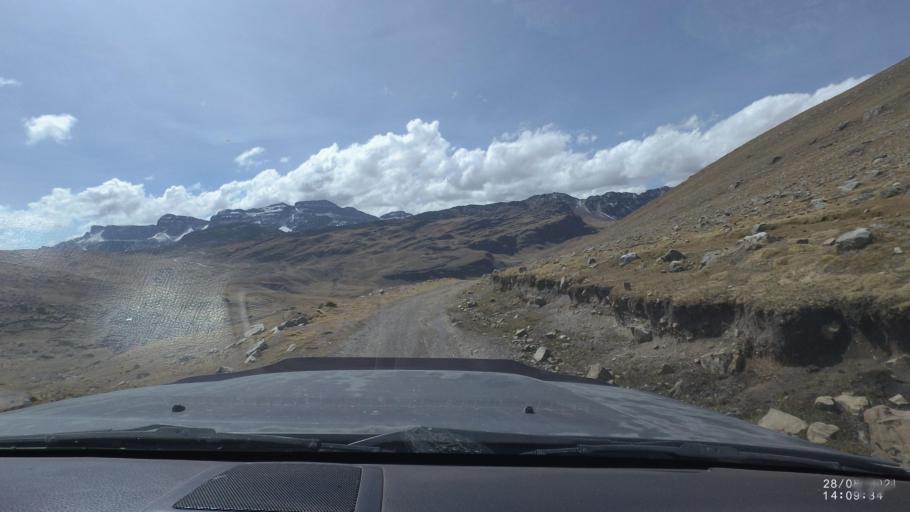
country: BO
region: Cochabamba
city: Sipe Sipe
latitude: -17.2622
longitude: -66.3836
